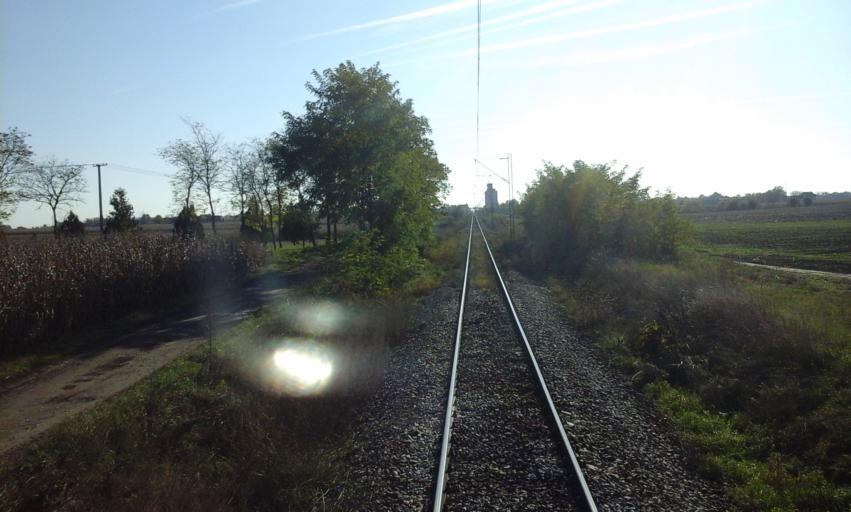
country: RS
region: Autonomna Pokrajina Vojvodina
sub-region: Severnobacki Okrug
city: Backa Topola
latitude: 45.9549
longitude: 19.6706
